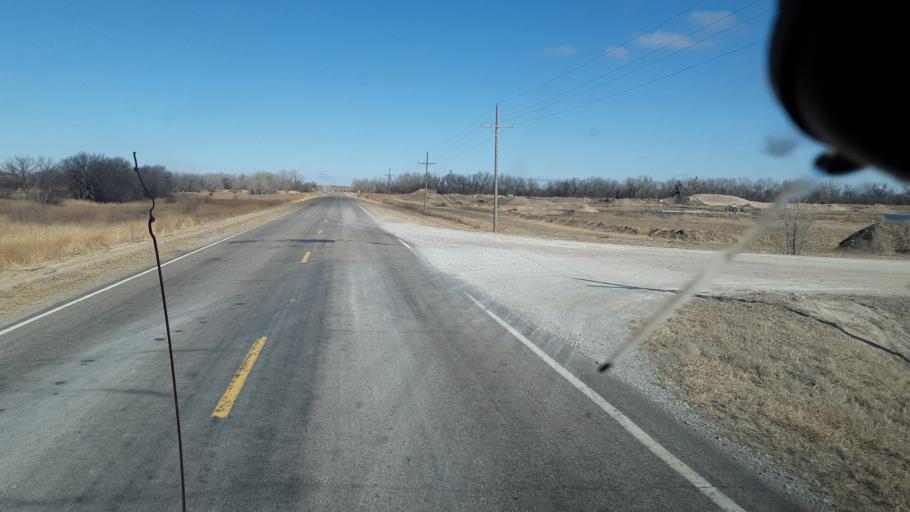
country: US
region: Kansas
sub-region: Barton County
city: Ellinwood
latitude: 38.3506
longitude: -98.6642
